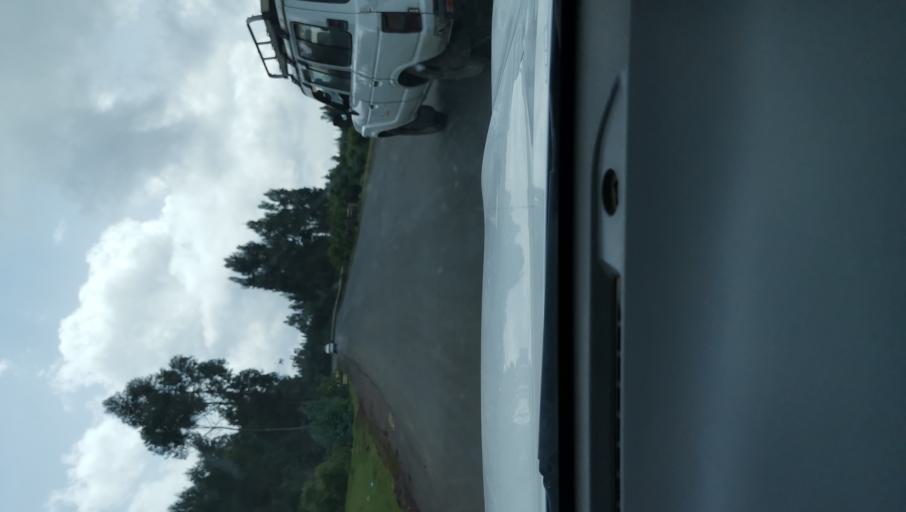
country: ET
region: Oromiya
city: Gedo
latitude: 8.9864
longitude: 37.4655
